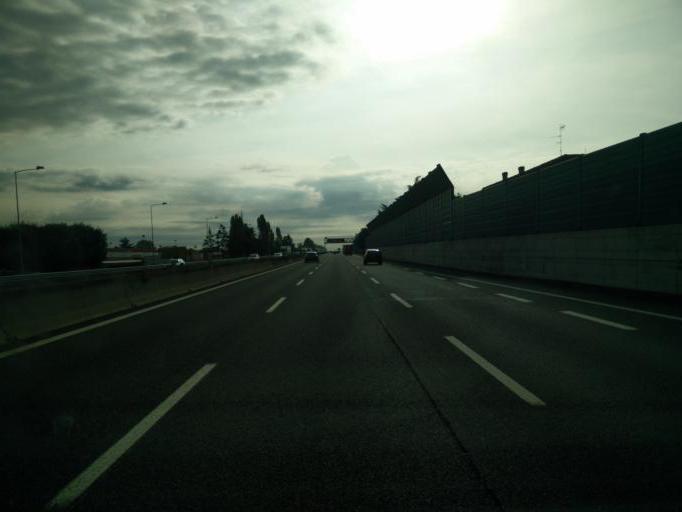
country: IT
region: Lombardy
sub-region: Provincia di Brescia
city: Roncadelle
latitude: 45.5308
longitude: 10.1533
